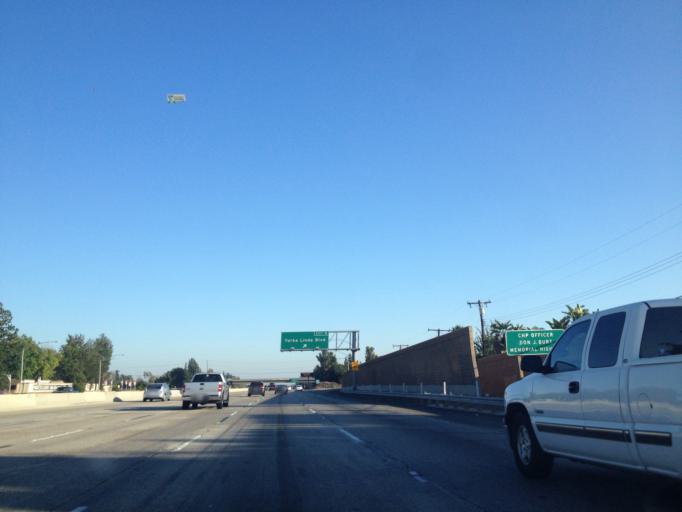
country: US
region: California
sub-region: Orange County
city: Placentia
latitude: 33.8938
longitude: -117.8809
